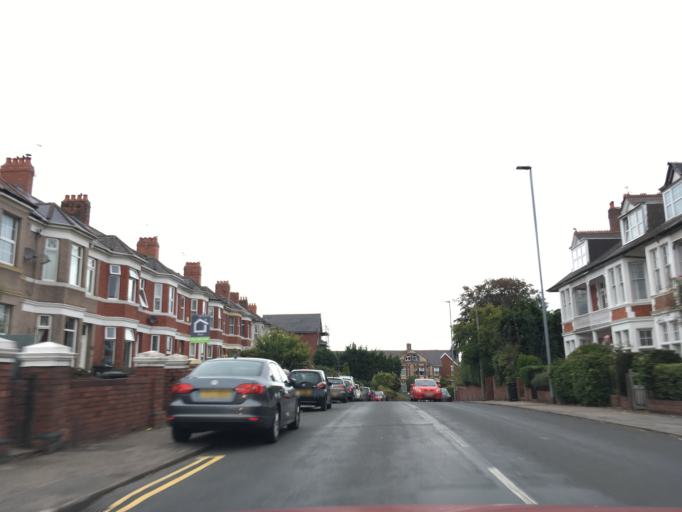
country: GB
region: Wales
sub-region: Newport
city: Newport
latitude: 51.5820
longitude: -3.0128
